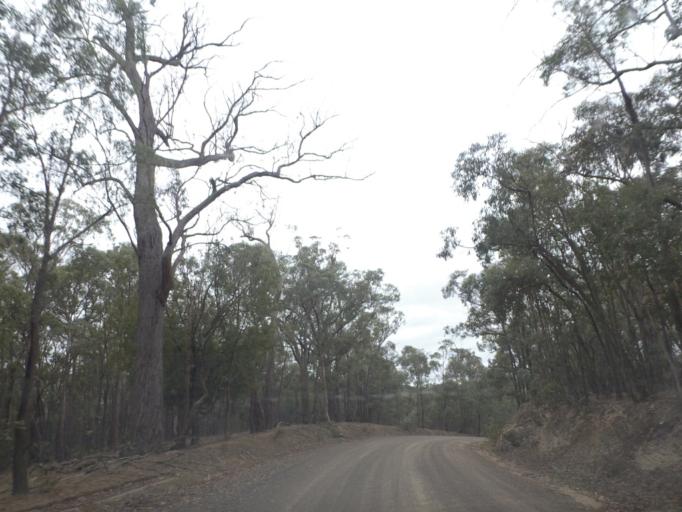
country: AU
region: Victoria
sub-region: Yarra Ranges
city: Yarra Glen
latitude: -37.6759
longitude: 145.3314
